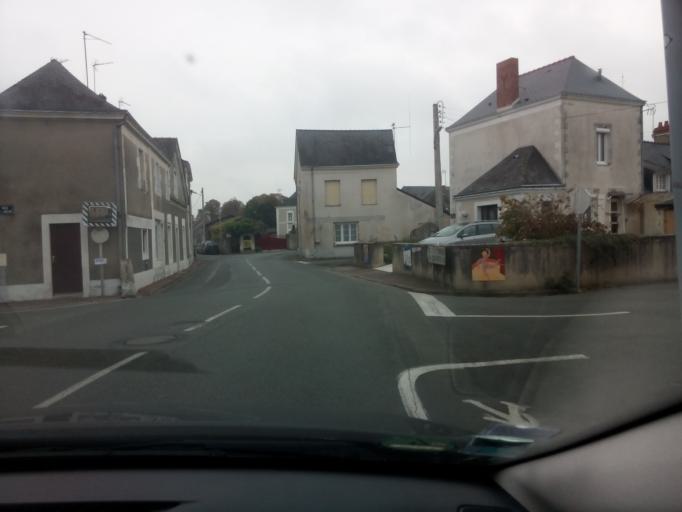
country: FR
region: Pays de la Loire
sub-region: Departement de Maine-et-Loire
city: Tierce
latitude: 47.6213
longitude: -0.5088
